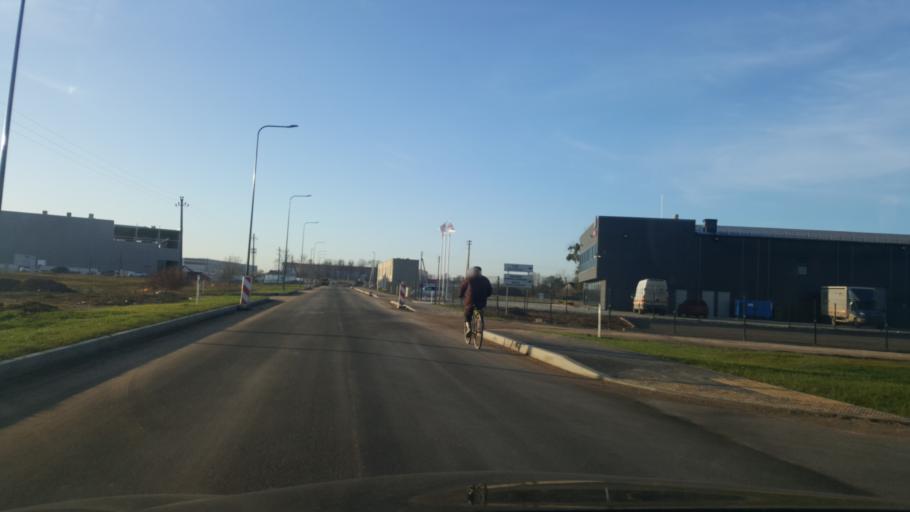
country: LT
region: Kauno apskritis
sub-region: Kauno rajonas
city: Mastaiciai
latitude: 54.8535
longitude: 23.8477
